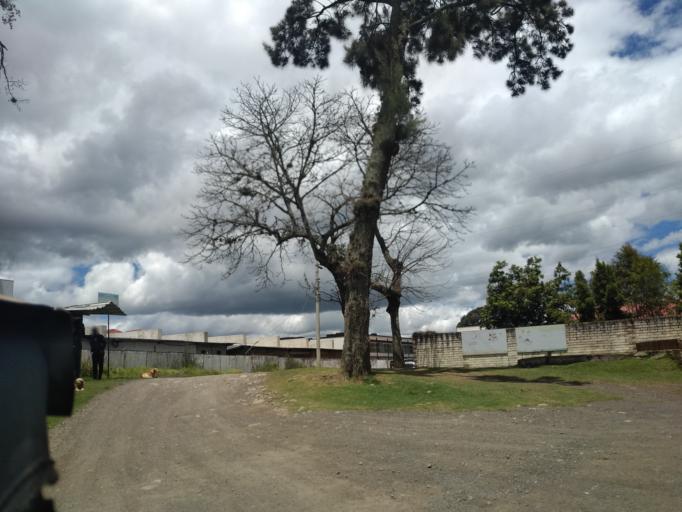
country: EC
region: Azuay
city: Cuenca
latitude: -2.8912
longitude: -79.0360
